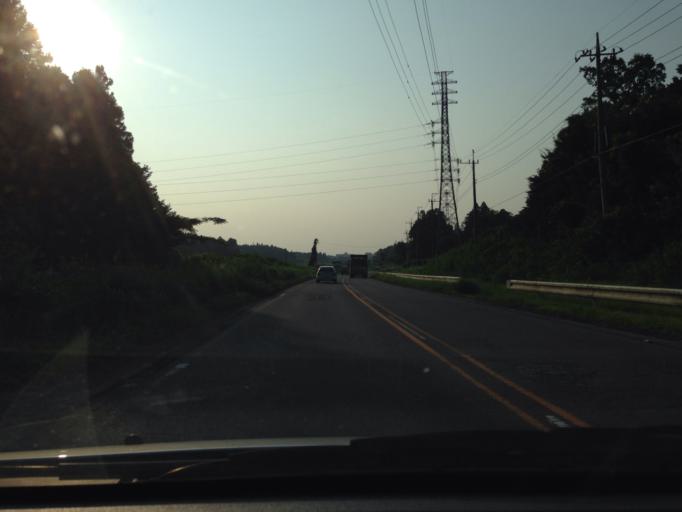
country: JP
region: Ibaraki
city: Ami
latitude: 36.0228
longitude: 140.2397
